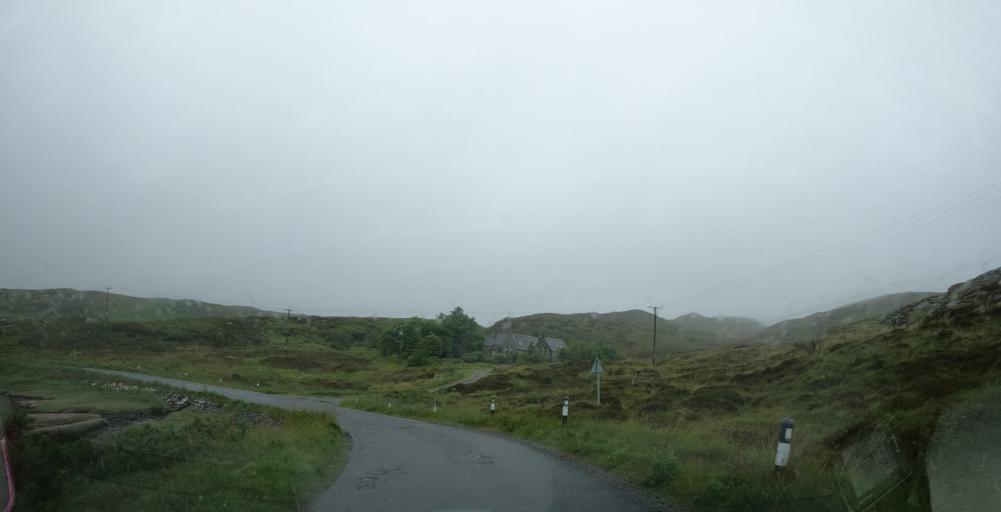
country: GB
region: Scotland
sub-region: Eilean Siar
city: Barra
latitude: 56.9920
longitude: -7.4218
